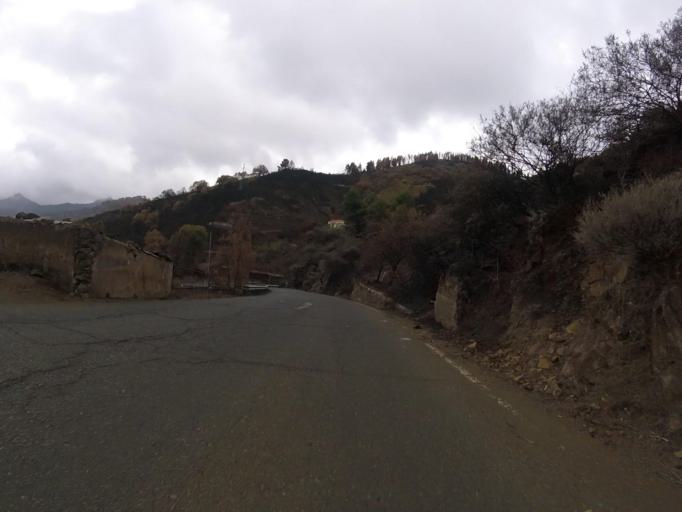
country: ES
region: Canary Islands
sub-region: Provincia de Las Palmas
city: Tejeda
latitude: 27.9848
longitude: -15.5763
